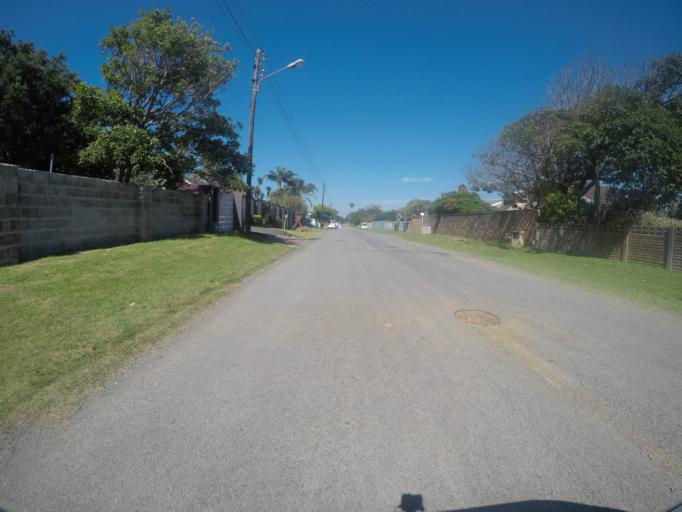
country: ZA
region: Eastern Cape
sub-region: Buffalo City Metropolitan Municipality
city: East London
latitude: -32.9477
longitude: 28.0082
